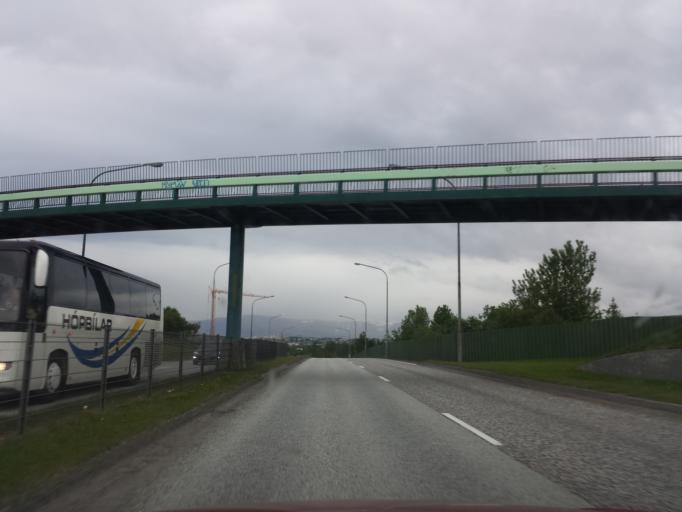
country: IS
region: Capital Region
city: Gardabaer
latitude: 64.0863
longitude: -21.9377
